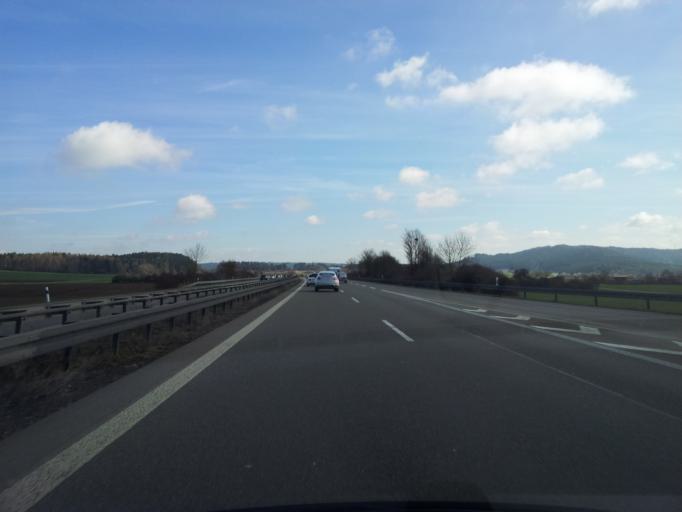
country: DE
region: Baden-Wuerttemberg
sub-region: Freiburg Region
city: Dietingen
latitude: 48.2081
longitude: 8.6283
